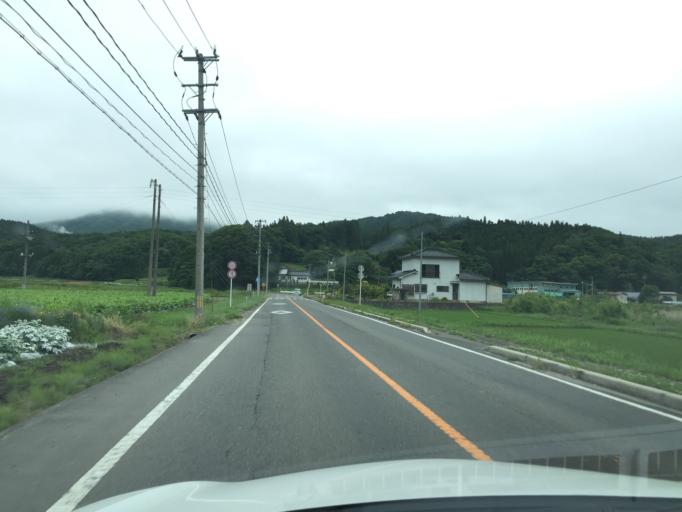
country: JP
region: Fukushima
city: Funehikimachi-funehiki
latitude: 37.2977
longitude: 140.6521
